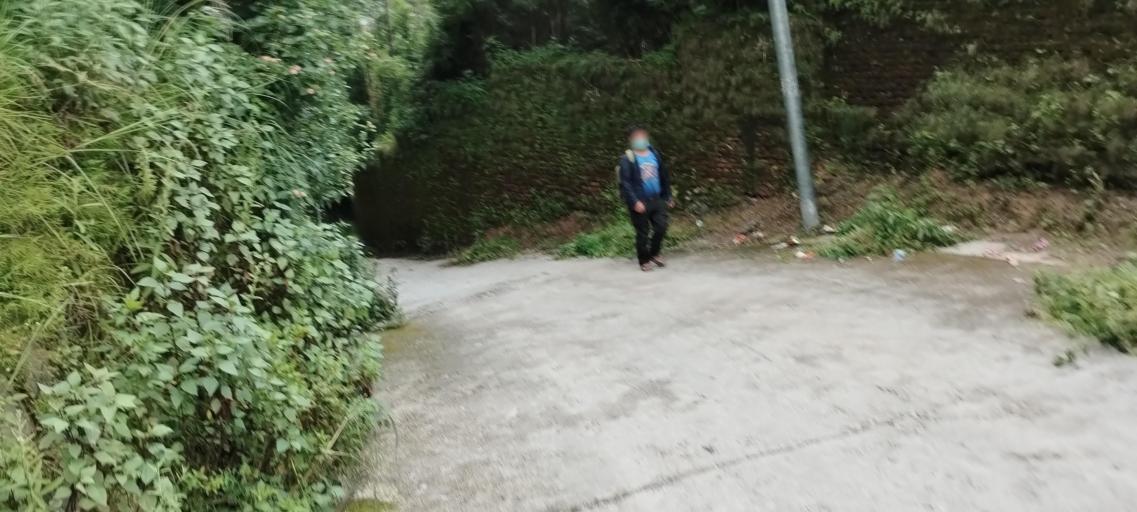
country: NP
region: Central Region
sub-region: Bagmati Zone
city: Kathmandu
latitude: 27.7865
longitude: 85.3599
